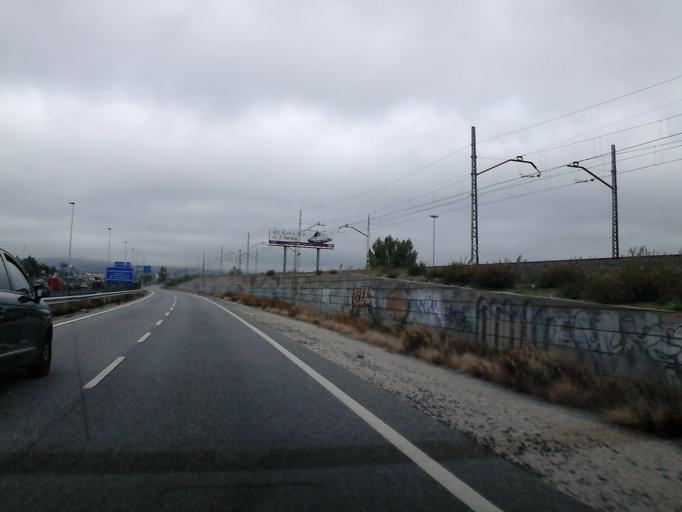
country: ES
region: Madrid
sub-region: Provincia de Madrid
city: Las Matas
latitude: 40.5329
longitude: -3.8874
